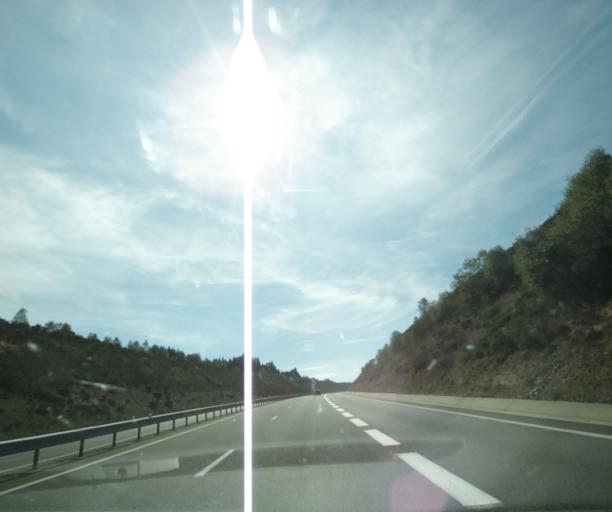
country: FR
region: Auvergne
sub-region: Departement du Puy-de-Dome
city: Gelles
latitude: 45.8001
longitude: 2.7670
